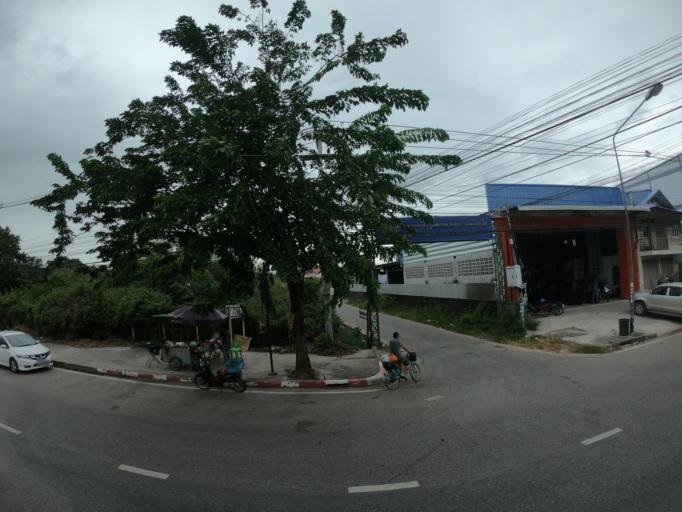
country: TH
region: Roi Et
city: Roi Et
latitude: 16.0472
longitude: 103.6372
